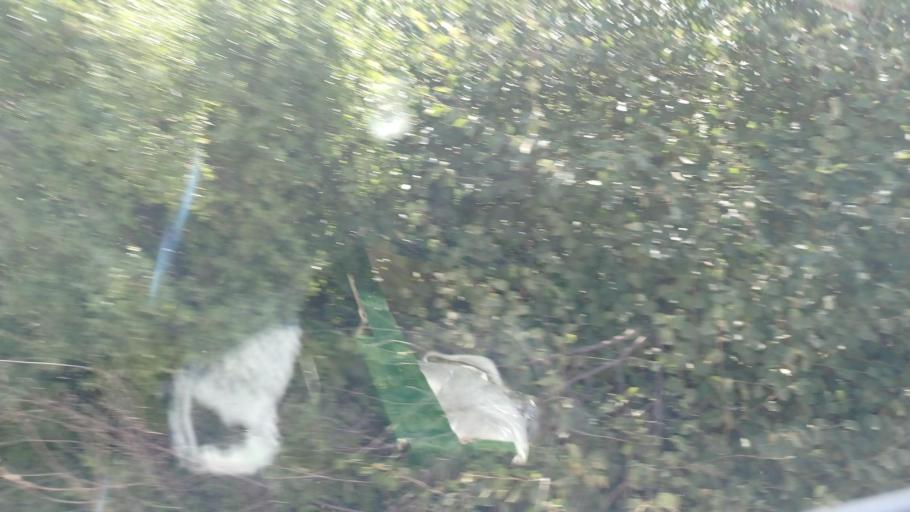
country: CY
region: Pafos
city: Mesogi
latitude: 34.9251
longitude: 32.6298
